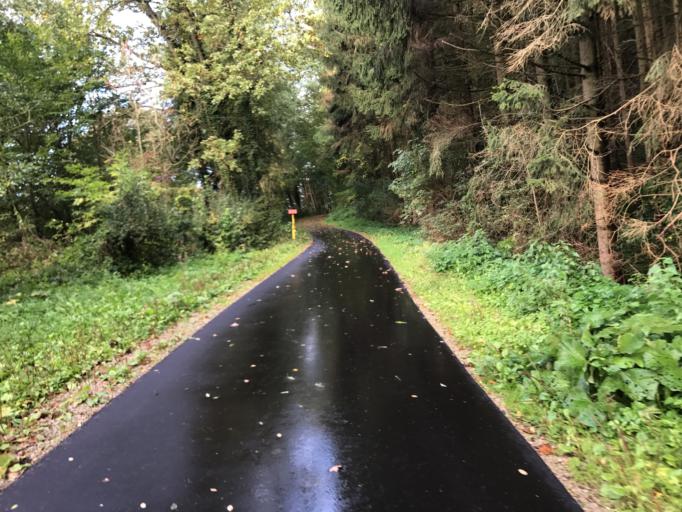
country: DE
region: Hesse
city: Witzenhausen
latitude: 51.3327
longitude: 9.8613
